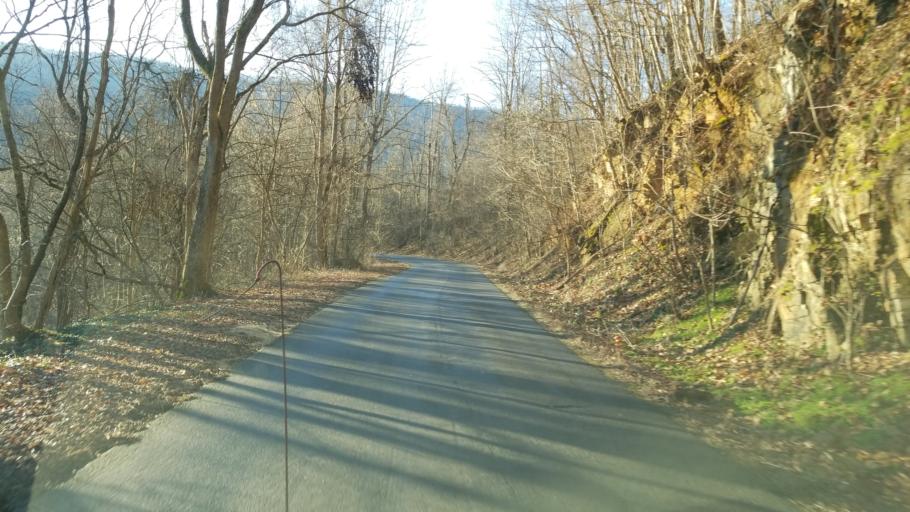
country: US
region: Virginia
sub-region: Pulaski County
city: Pulaski
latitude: 37.1660
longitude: -80.8599
